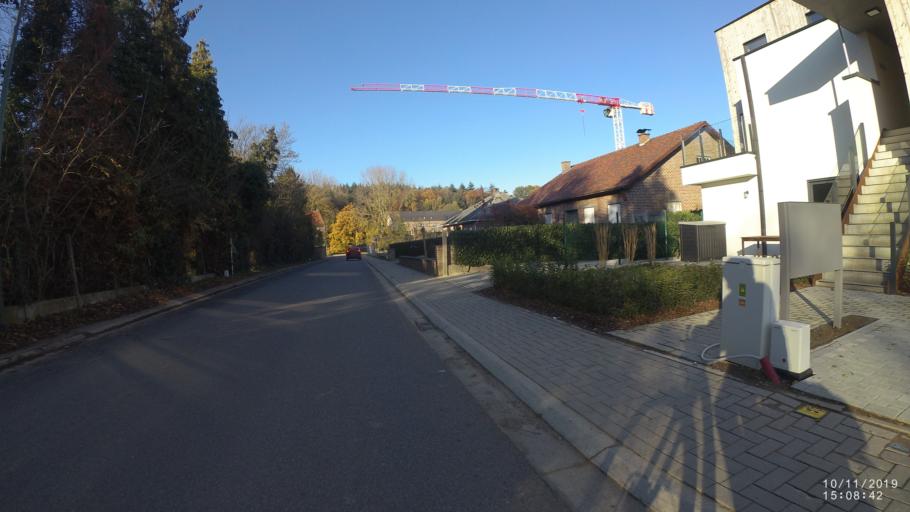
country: BE
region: Flanders
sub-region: Provincie Vlaams-Brabant
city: Lubbeek
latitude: 50.9086
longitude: 4.8845
